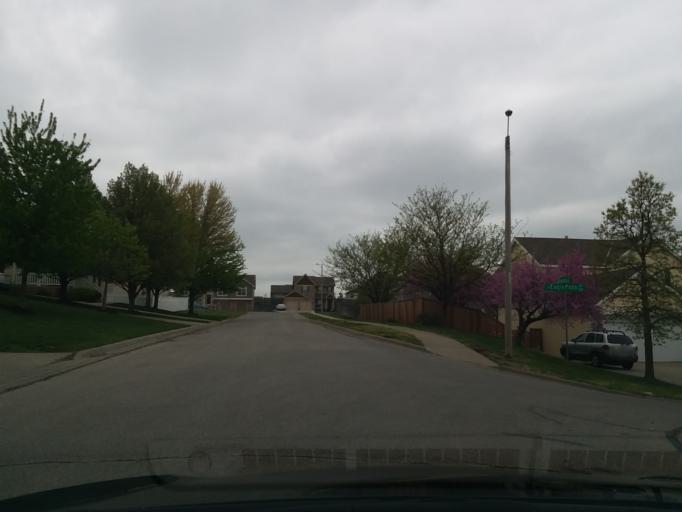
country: US
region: Kansas
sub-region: Douglas County
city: Lawrence
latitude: 38.9909
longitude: -95.2837
